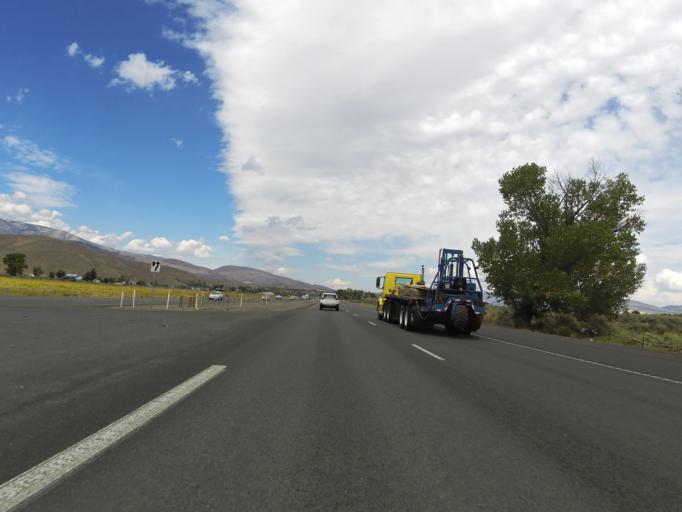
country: US
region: Nevada
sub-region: Douglas County
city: Indian Hills
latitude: 39.0495
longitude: -119.7798
